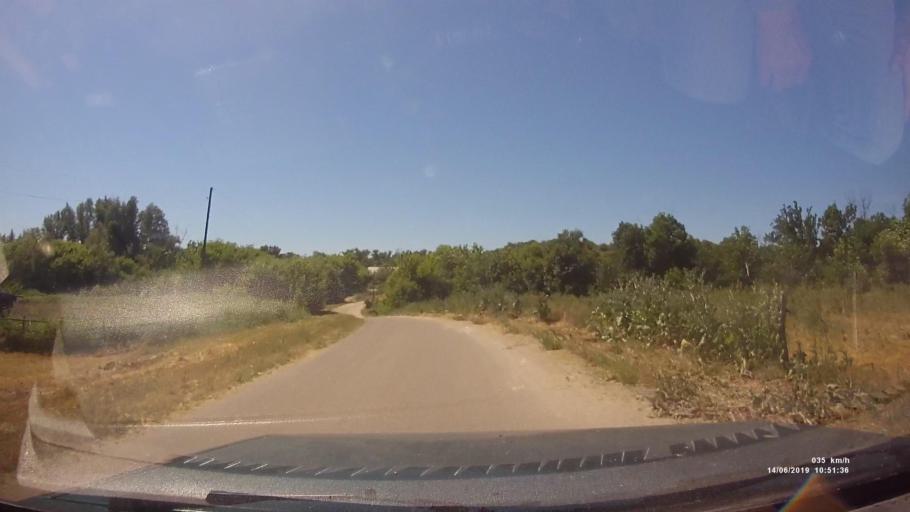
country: RU
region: Rostov
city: Kazanskaya
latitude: 49.8689
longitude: 41.3921
